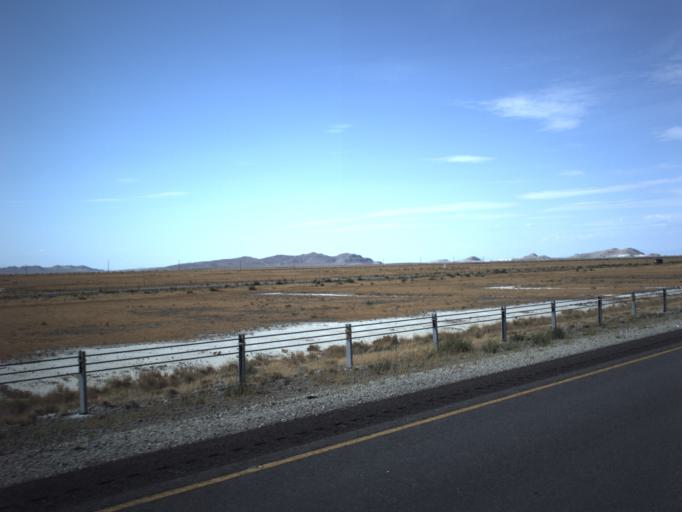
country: US
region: Utah
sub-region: Tooele County
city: Grantsville
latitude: 40.7267
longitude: -113.2045
